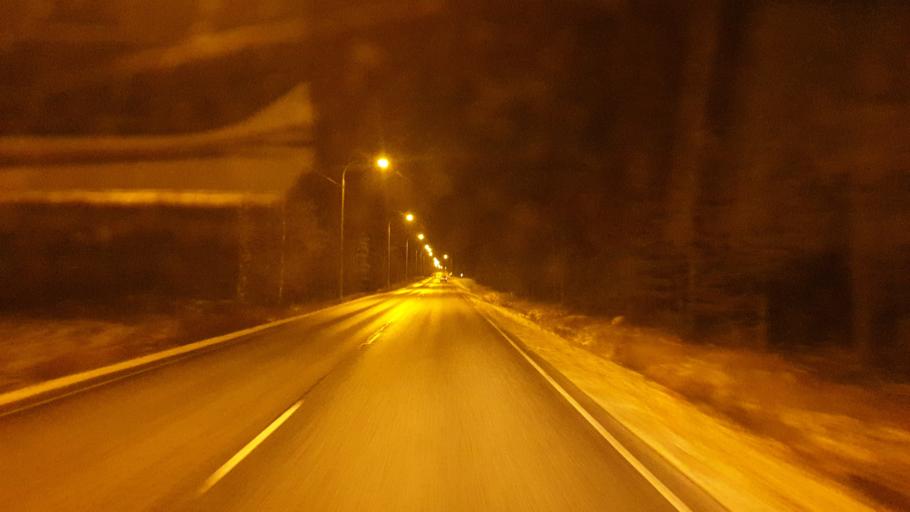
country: FI
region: Northern Savo
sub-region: Sisae-Savo
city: Suonenjoki
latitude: 62.6689
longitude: 27.3691
